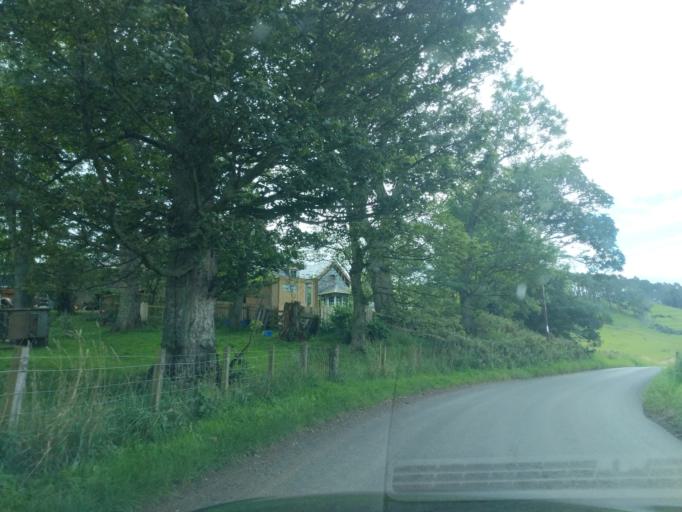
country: GB
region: Scotland
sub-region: The Scottish Borders
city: West Linton
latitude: 55.7132
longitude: -3.3353
